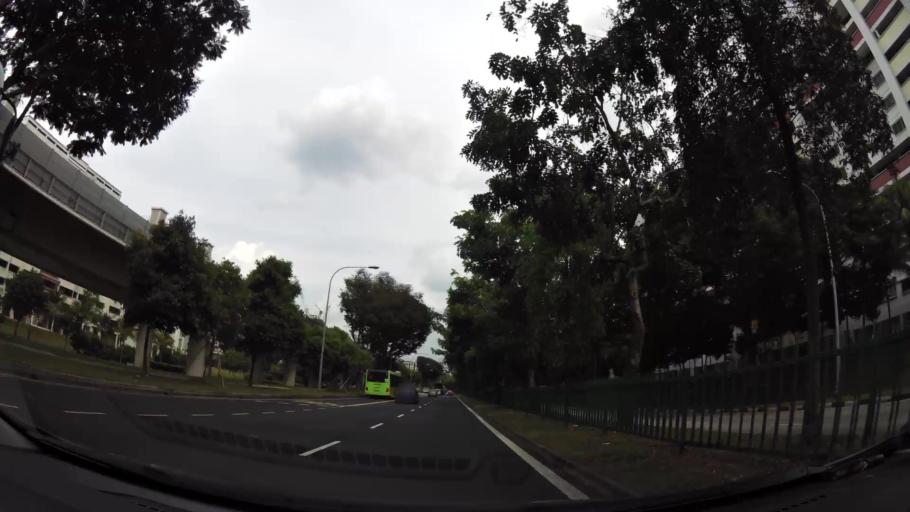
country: MY
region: Johor
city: Johor Bahru
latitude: 1.4323
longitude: 103.7759
